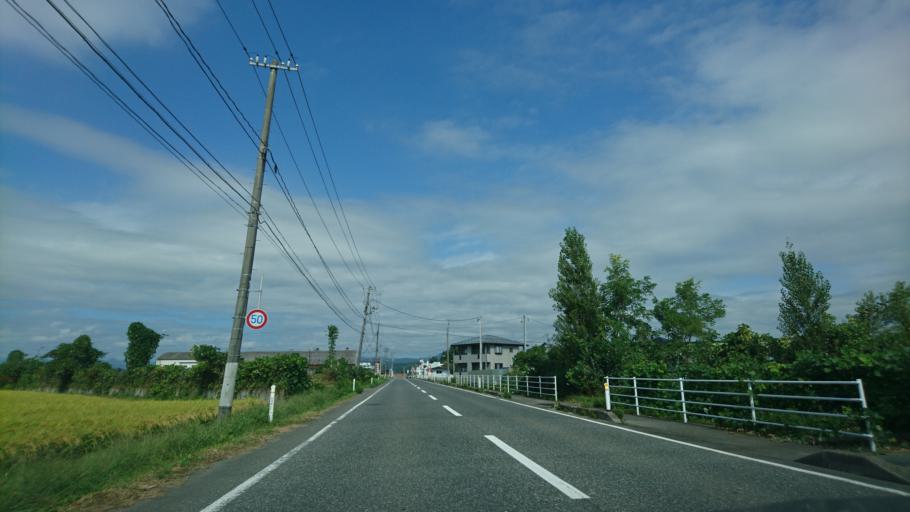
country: JP
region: Miyagi
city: Furukawa
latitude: 38.7371
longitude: 140.9511
